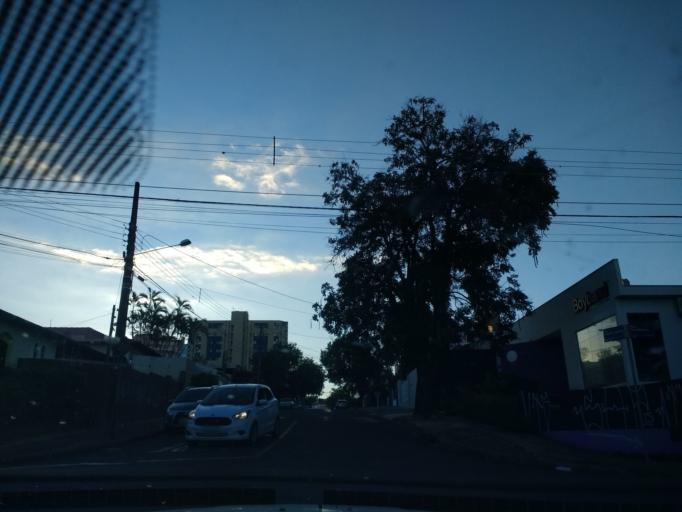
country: BR
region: Parana
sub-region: Londrina
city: Londrina
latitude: -23.3236
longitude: -51.1650
